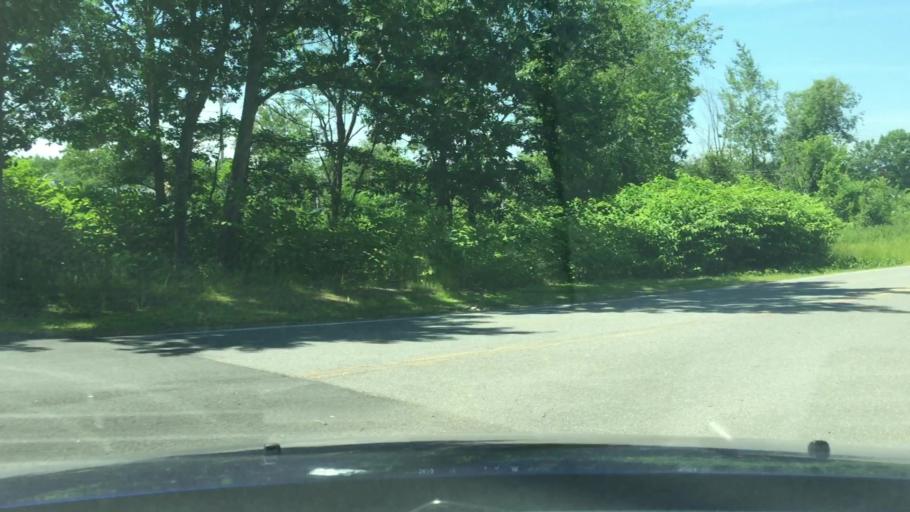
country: US
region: New Hampshire
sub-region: Rockingham County
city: Plaistow
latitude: 42.8211
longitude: -71.1036
